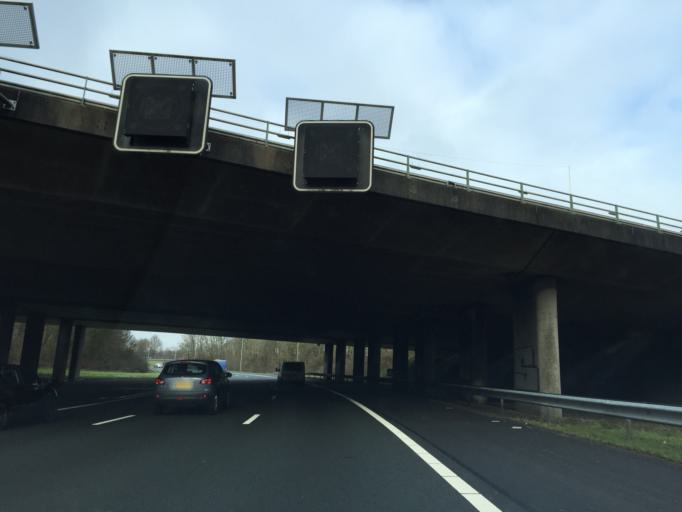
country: NL
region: Utrecht
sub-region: Gemeente Utrecht
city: Lunetten
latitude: 52.0555
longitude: 5.1481
